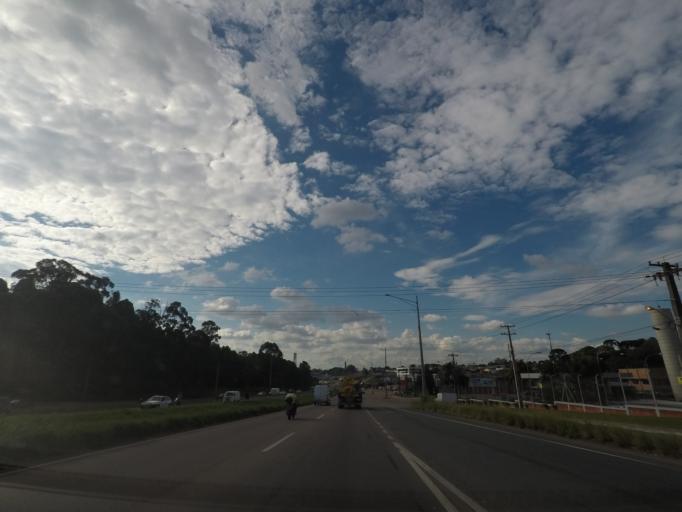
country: BR
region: Parana
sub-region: Sao Jose Dos Pinhais
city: Sao Jose dos Pinhais
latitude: -25.5411
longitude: -49.3024
